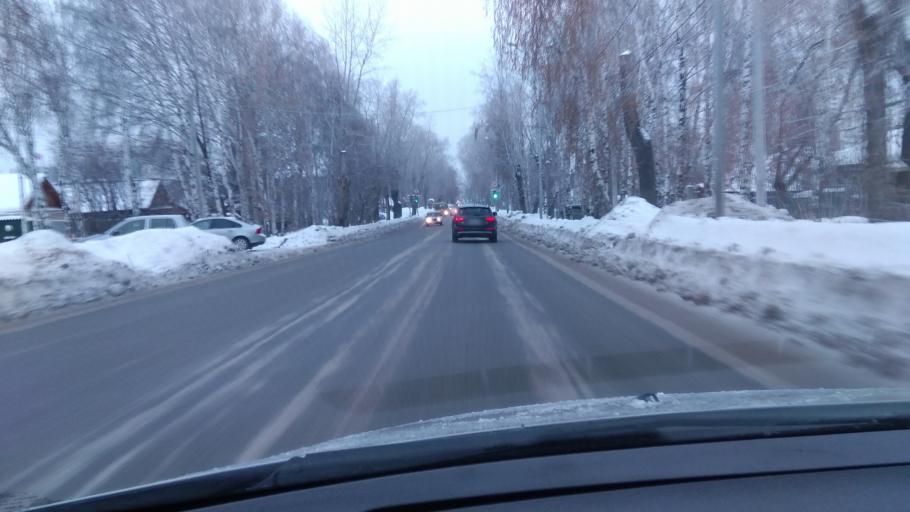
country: RU
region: Sverdlovsk
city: Yekaterinburg
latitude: 56.8079
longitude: 60.5881
